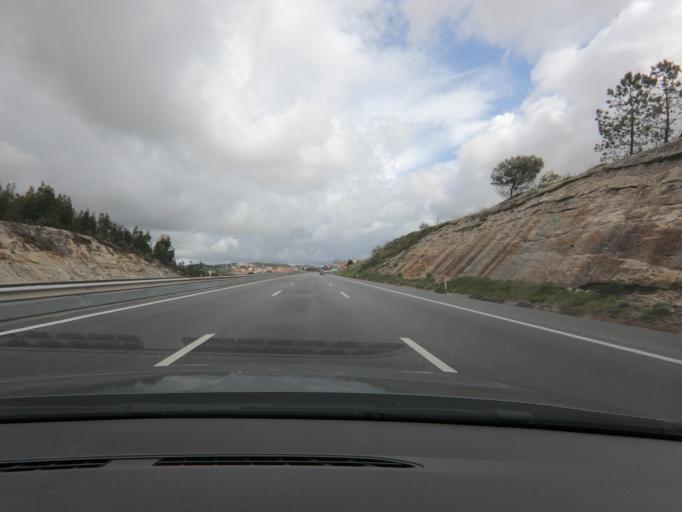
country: PT
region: Lisbon
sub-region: Odivelas
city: Canecas
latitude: 38.7979
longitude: -9.2387
